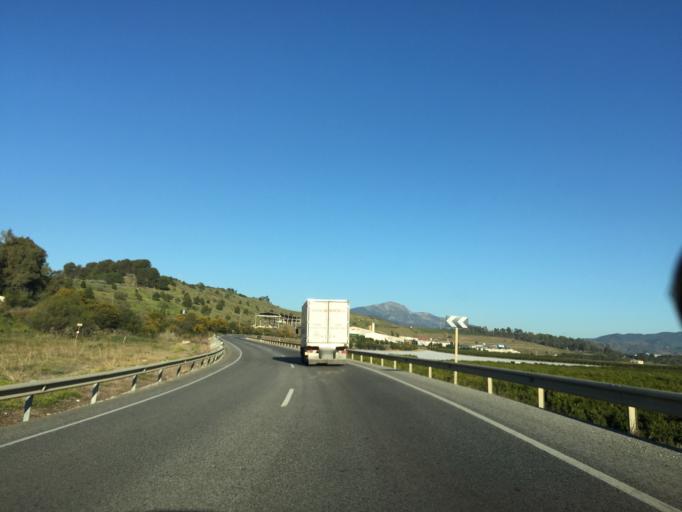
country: ES
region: Andalusia
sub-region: Provincia de Malaga
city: Pizarra
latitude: 36.7547
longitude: -4.7223
